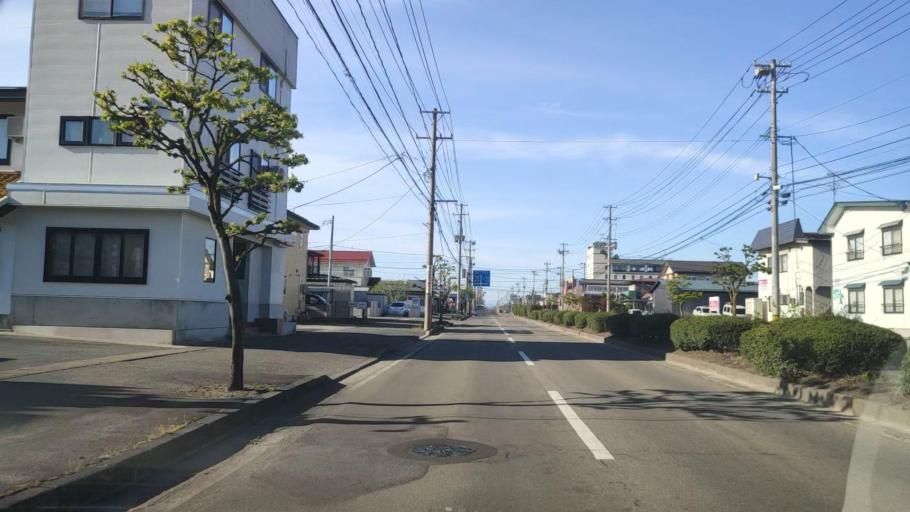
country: JP
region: Yamagata
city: Tendo
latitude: 38.3642
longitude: 140.3667
